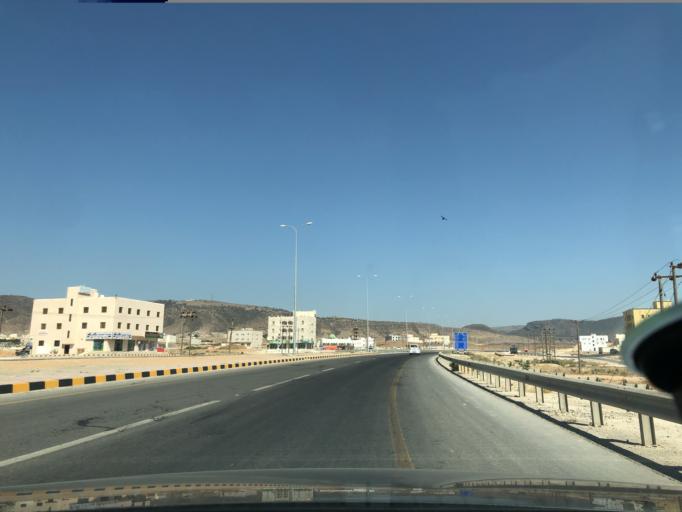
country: OM
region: Zufar
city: Salalah
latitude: 17.0504
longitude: 54.4002
